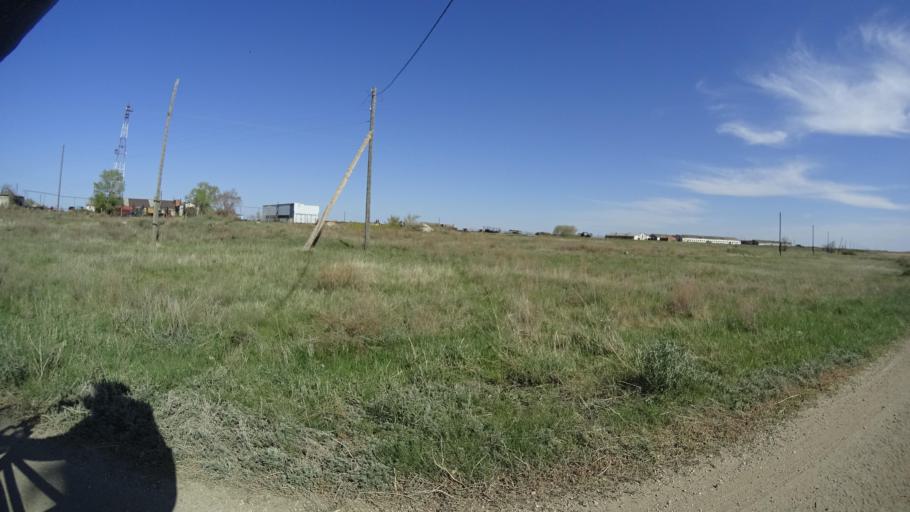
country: RU
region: Chelyabinsk
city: Chesma
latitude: 53.7875
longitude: 61.0397
